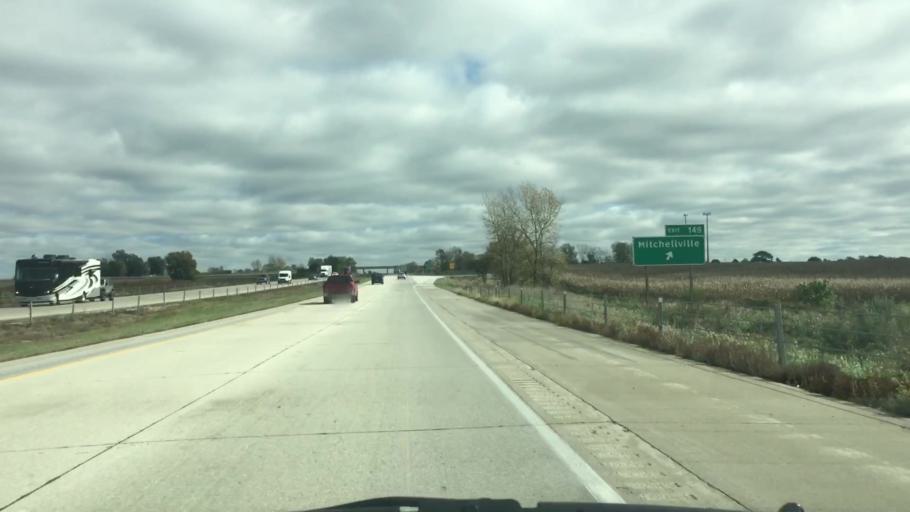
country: US
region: Iowa
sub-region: Polk County
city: Mitchellville
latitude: 41.6803
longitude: -93.3775
